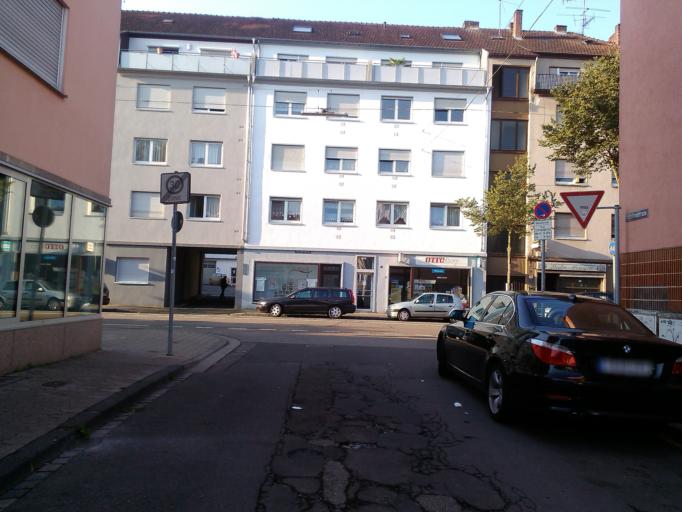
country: DE
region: Saarland
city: Saarbrucken
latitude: 49.2320
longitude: 6.9780
